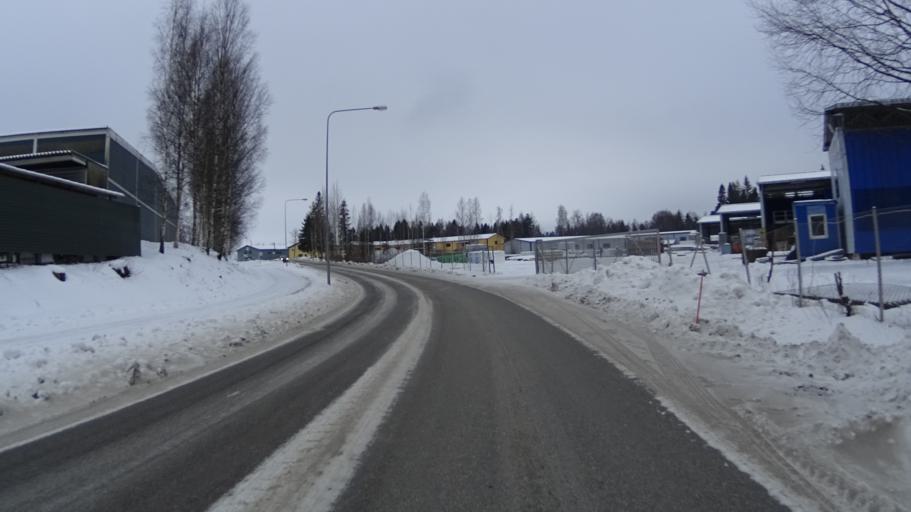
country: FI
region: Uusimaa
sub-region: Helsinki
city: Karkkila
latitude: 60.5250
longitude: 24.2370
